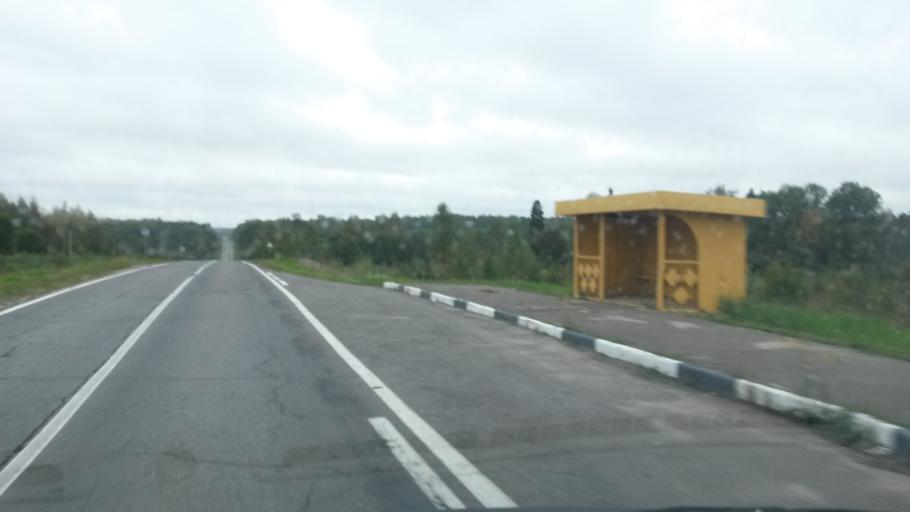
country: RU
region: Jaroslavl
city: Tutayev
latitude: 57.9511
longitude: 39.4291
